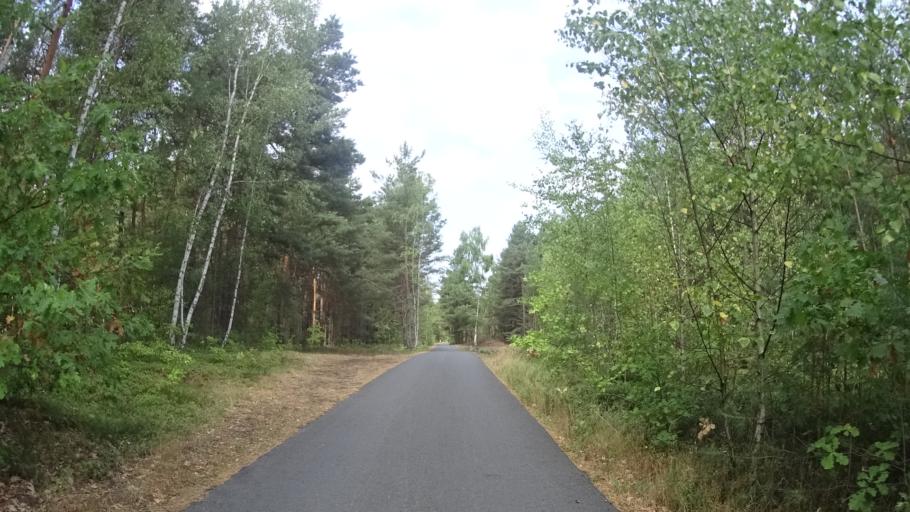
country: DE
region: Brandenburg
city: Tschernitz
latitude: 51.5873
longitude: 14.6023
